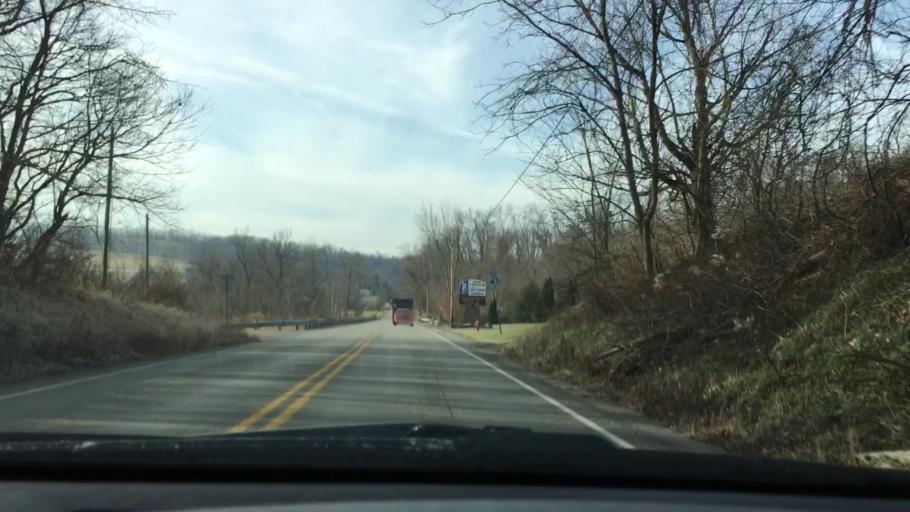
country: US
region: Pennsylvania
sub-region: Allegheny County
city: Industry
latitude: 40.2490
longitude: -79.7791
